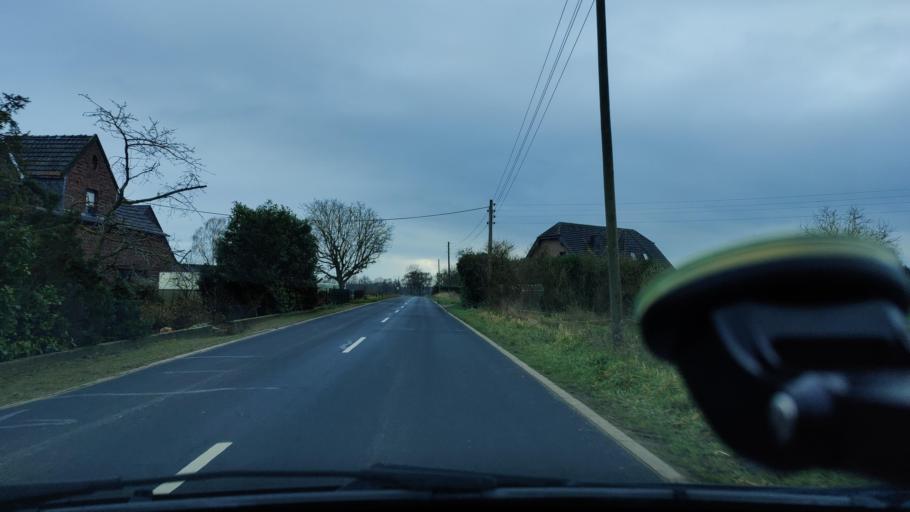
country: DE
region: North Rhine-Westphalia
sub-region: Regierungsbezirk Dusseldorf
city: Alpen
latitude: 51.6111
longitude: 6.4766
